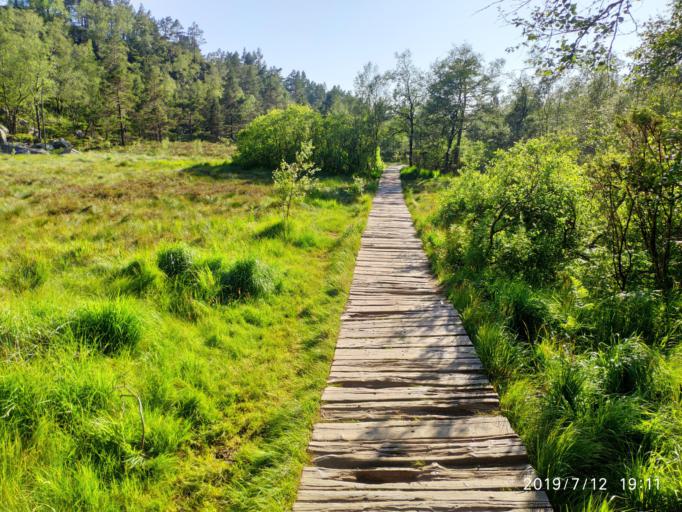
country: NO
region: Rogaland
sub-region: Forsand
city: Forsand
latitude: 58.9901
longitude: 6.1609
